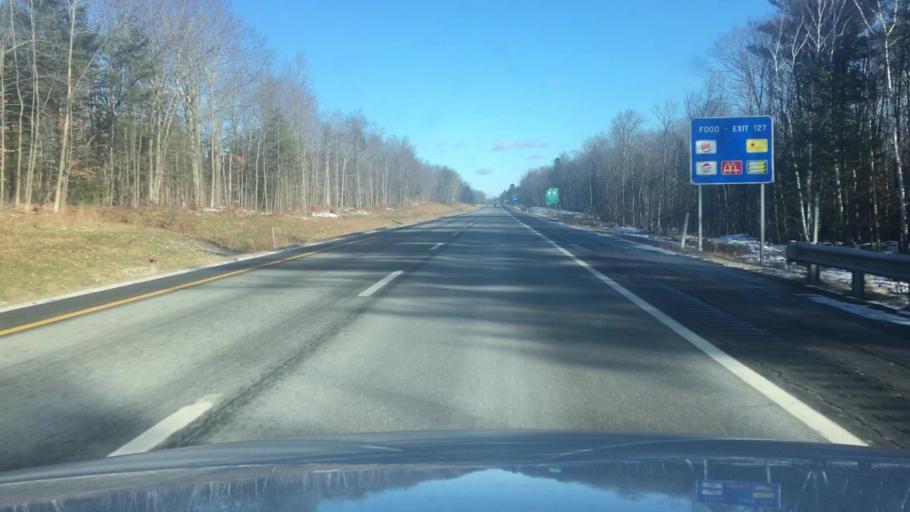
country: US
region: Maine
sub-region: Kennebec County
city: Oakland
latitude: 44.5307
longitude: -69.6907
